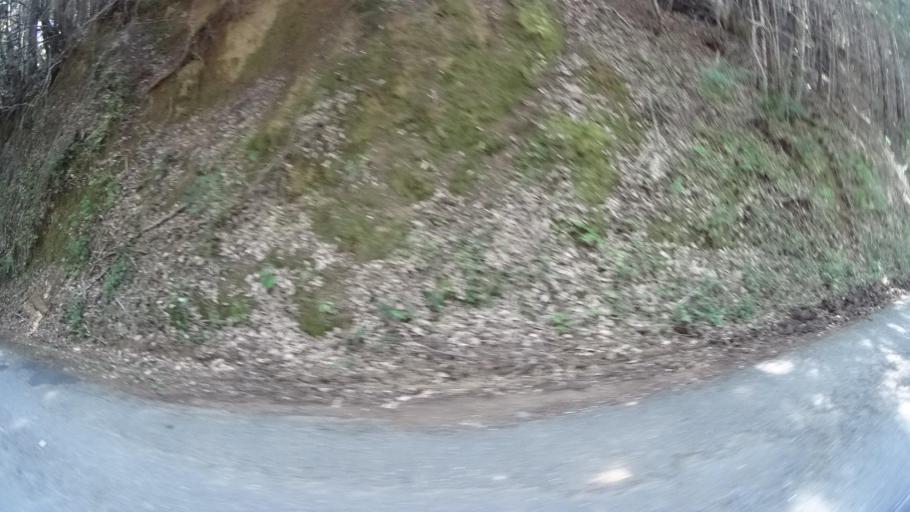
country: US
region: California
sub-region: Humboldt County
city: Redway
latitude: 40.2325
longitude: -123.6454
